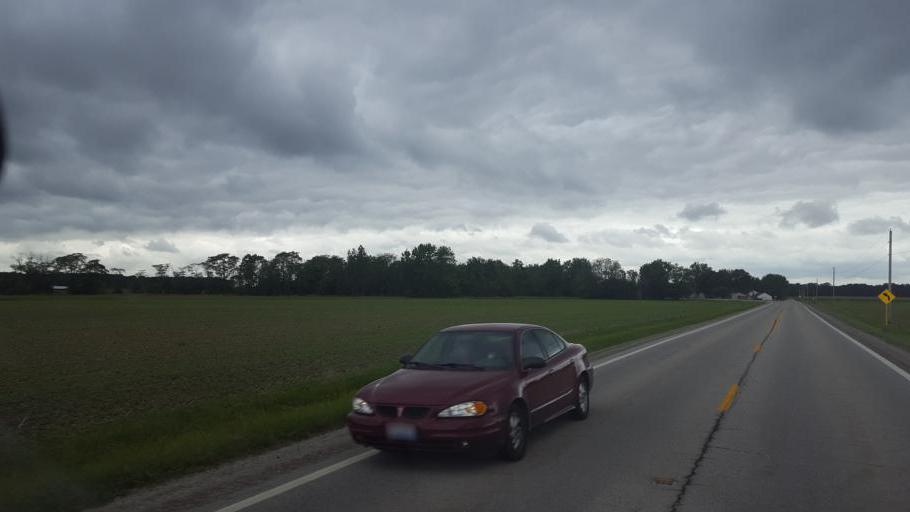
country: US
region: Ohio
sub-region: Marion County
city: Marion
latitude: 40.6666
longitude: -83.1448
